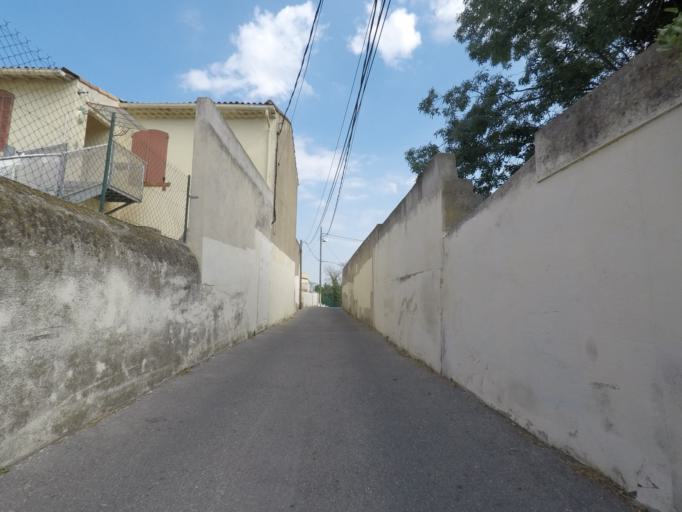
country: FR
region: Provence-Alpes-Cote d'Azur
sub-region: Departement des Bouches-du-Rhone
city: Marseille 10
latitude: 43.2628
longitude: 5.4221
